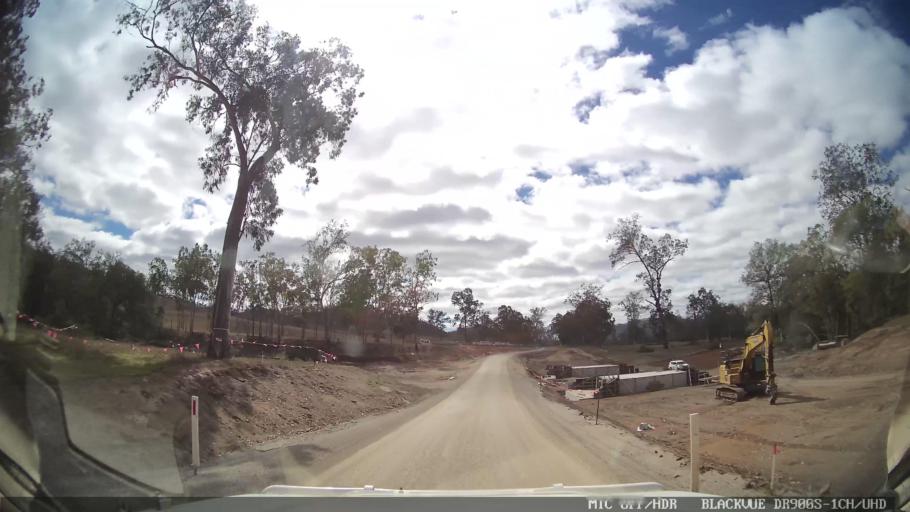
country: AU
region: Queensland
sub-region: Gladstone
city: Toolooa
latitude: -24.6147
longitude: 151.2991
